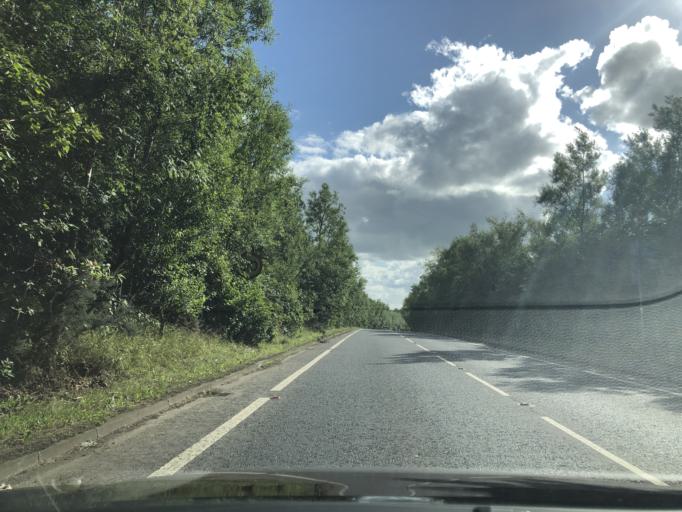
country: GB
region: Northern Ireland
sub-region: Ards District
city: Comber
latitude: 54.5506
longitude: -5.7308
